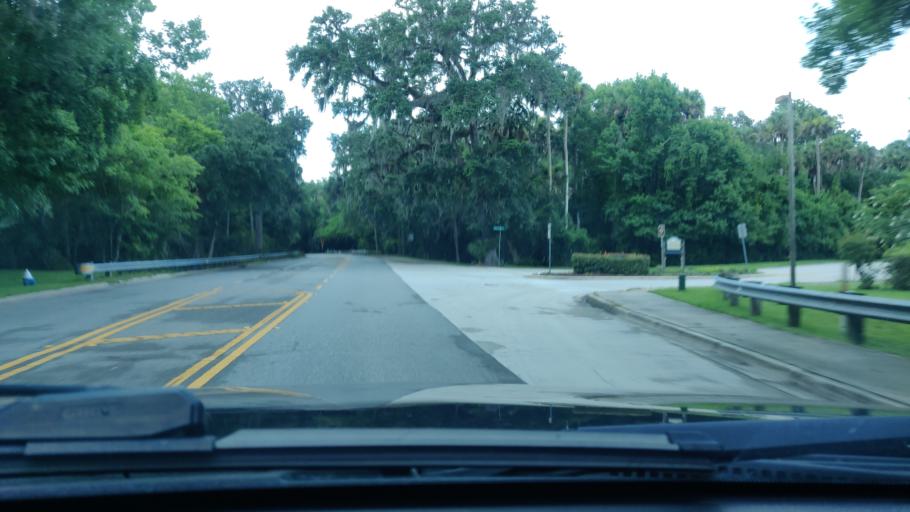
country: US
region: Florida
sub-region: Flagler County
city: Palm Coast
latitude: 29.5586
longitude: -81.1976
